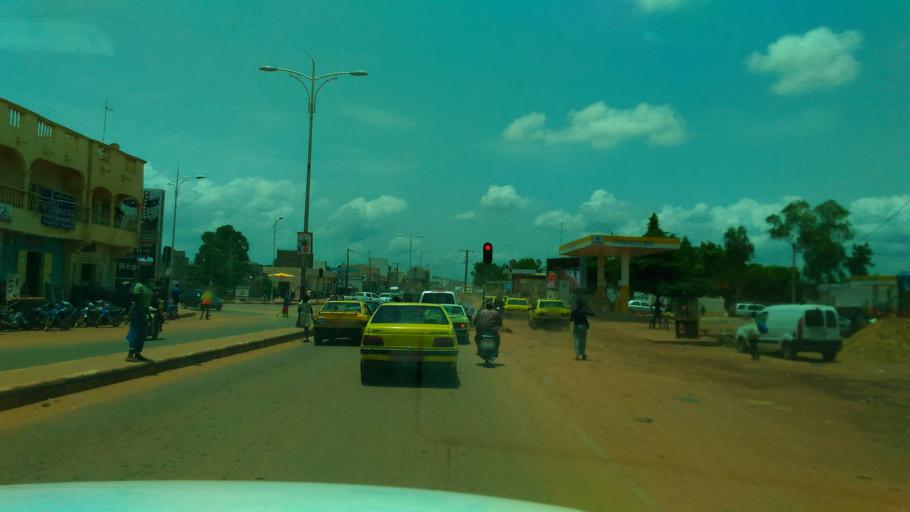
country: ML
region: Bamako
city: Bamako
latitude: 12.6664
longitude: -7.9315
